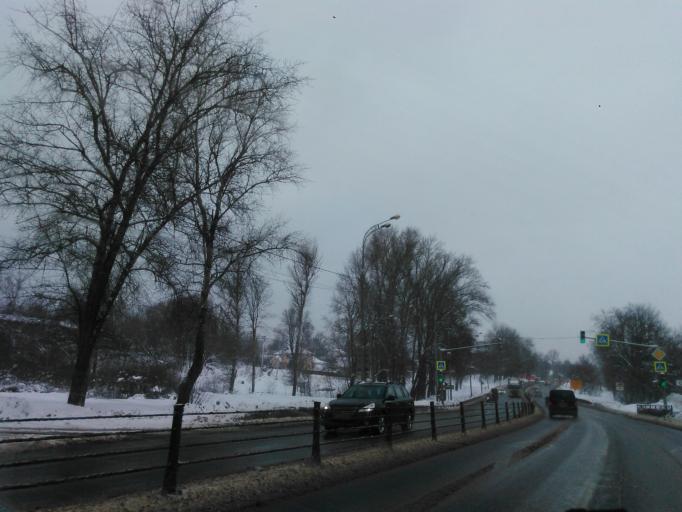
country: RU
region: Moskovskaya
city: Iksha
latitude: 56.1689
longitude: 37.5057
